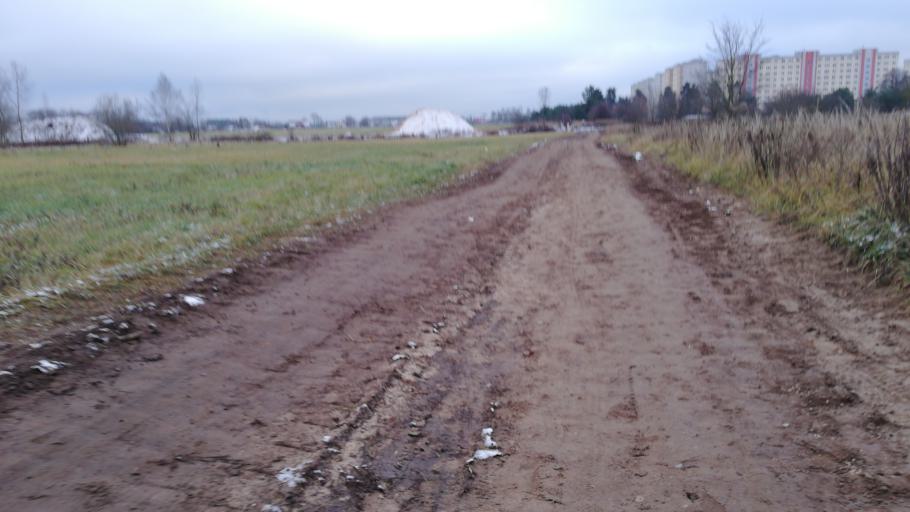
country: LV
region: Stopini
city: Ulbroka
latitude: 56.9504
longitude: 24.2376
